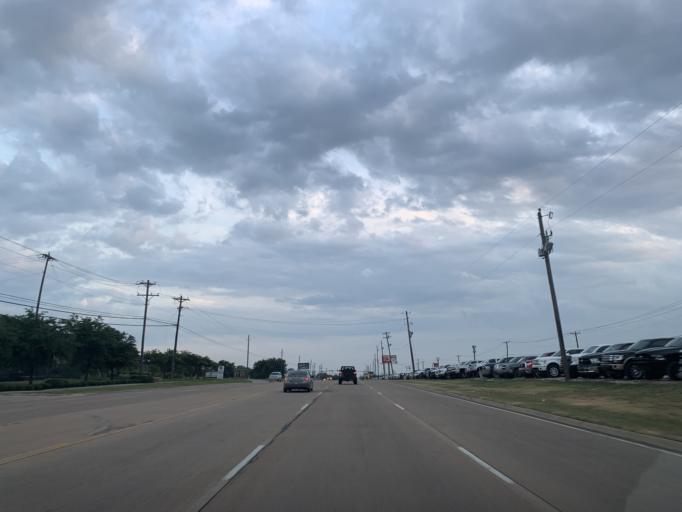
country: US
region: Texas
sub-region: Tarrant County
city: Keller
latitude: 32.9146
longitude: -97.2556
